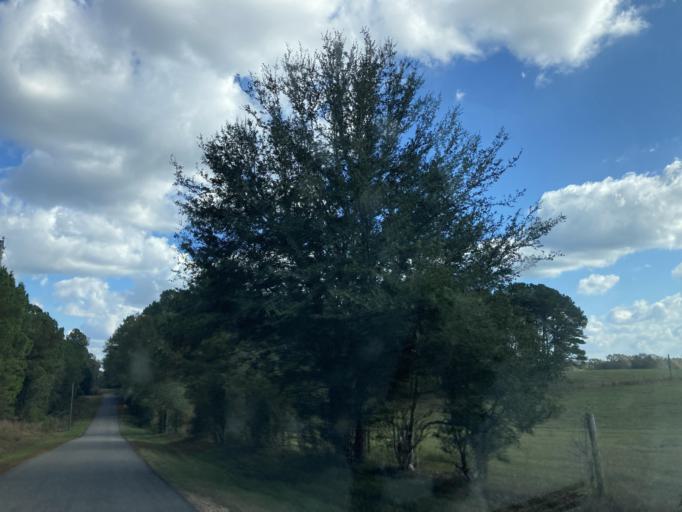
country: US
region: Mississippi
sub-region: Lamar County
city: Sumrall
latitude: 31.3756
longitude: -89.5492
